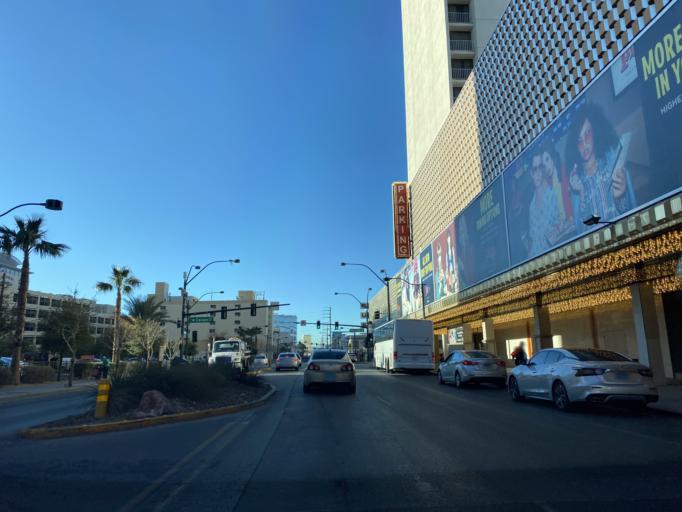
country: US
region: Nevada
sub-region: Clark County
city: Las Vegas
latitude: 36.1712
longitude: -115.1467
